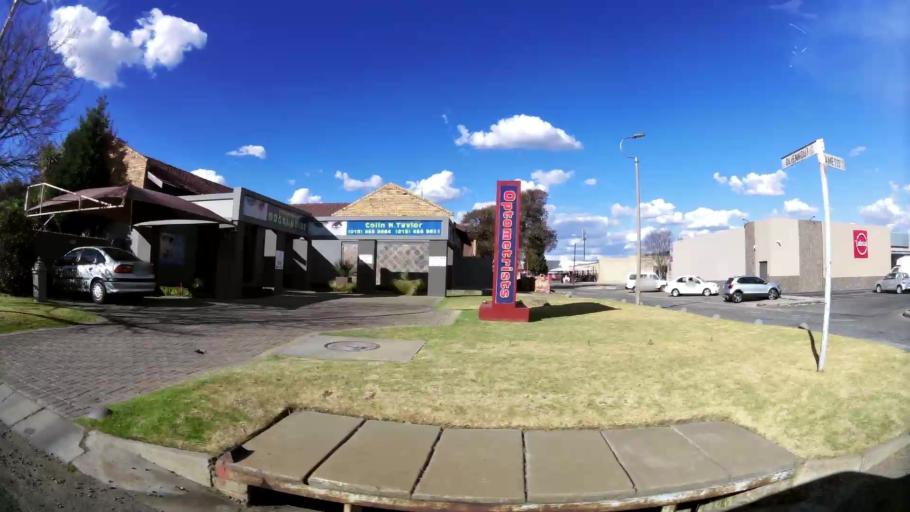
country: ZA
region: North-West
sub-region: Dr Kenneth Kaunda District Municipality
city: Klerksdorp
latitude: -26.8354
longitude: 26.6786
